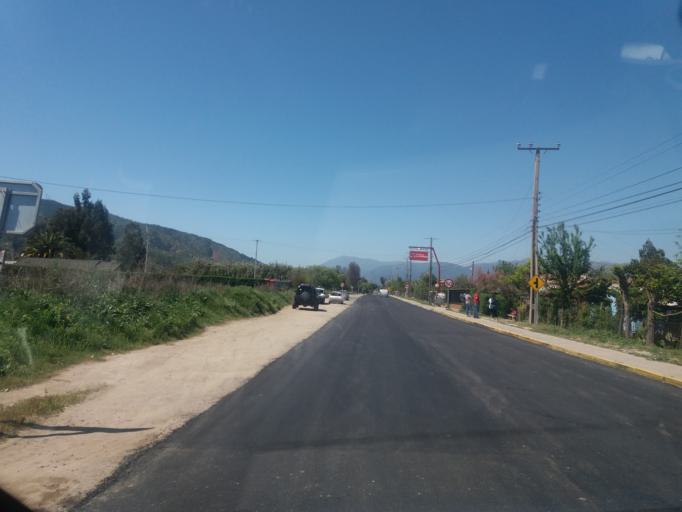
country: CL
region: Valparaiso
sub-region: Provincia de Marga Marga
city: Limache
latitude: -32.9738
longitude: -71.2962
